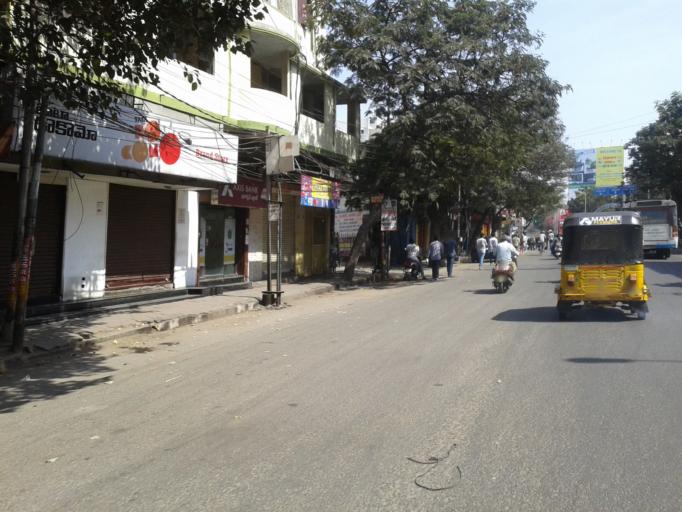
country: IN
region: Telangana
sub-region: Hyderabad
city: Hyderabad
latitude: 17.3851
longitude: 78.4833
